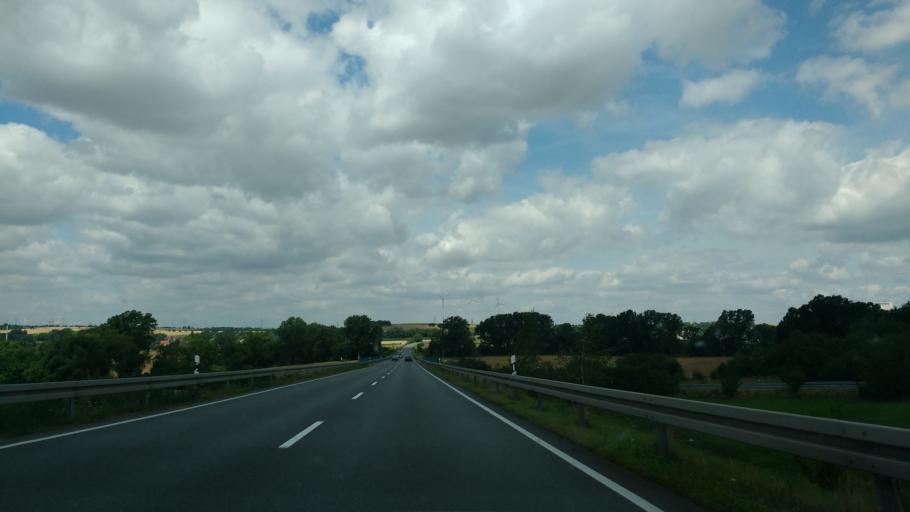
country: DE
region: Saxony-Anhalt
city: Zeitz
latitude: 51.0380
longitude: 12.1142
